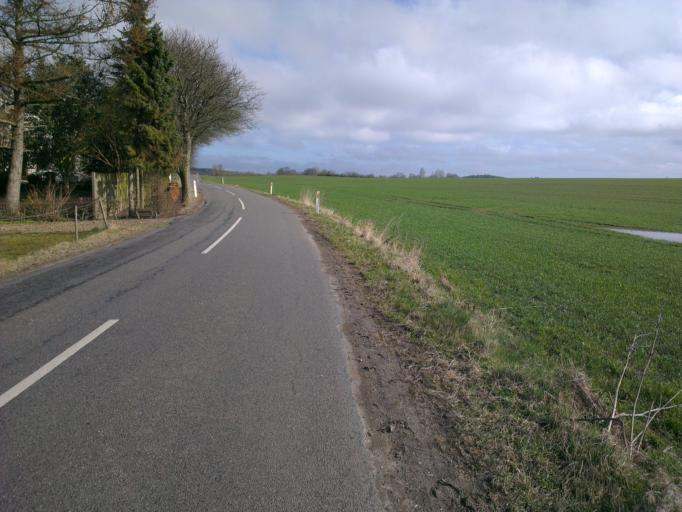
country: DK
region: Capital Region
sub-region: Hillerod Kommune
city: Skaevinge
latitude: 55.8763
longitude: 12.1208
